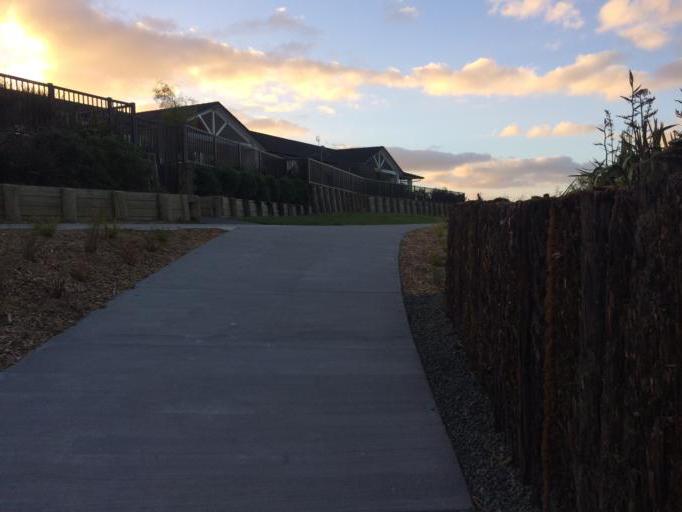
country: NZ
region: Auckland
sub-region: Auckland
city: Rosebank
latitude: -36.7891
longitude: 174.6606
